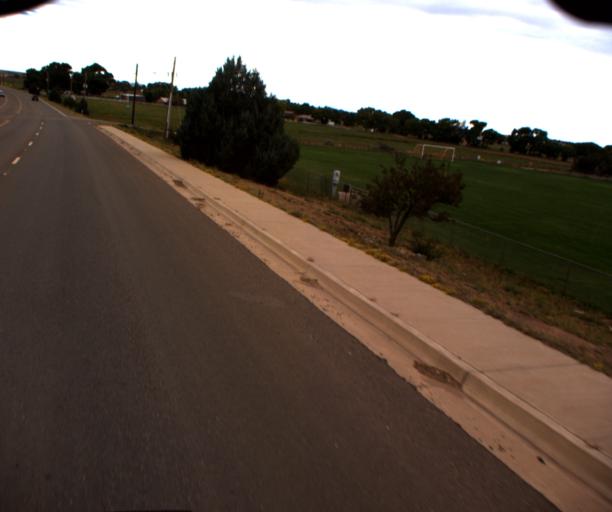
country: US
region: Arizona
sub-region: Navajo County
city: Snowflake
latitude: 34.4896
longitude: -110.0818
